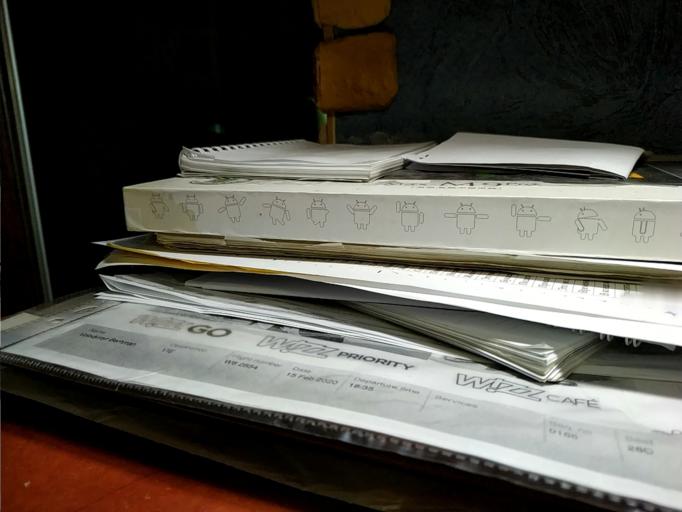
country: RU
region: Arkhangelskaya
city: Onega
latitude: 63.7834
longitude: 37.9788
